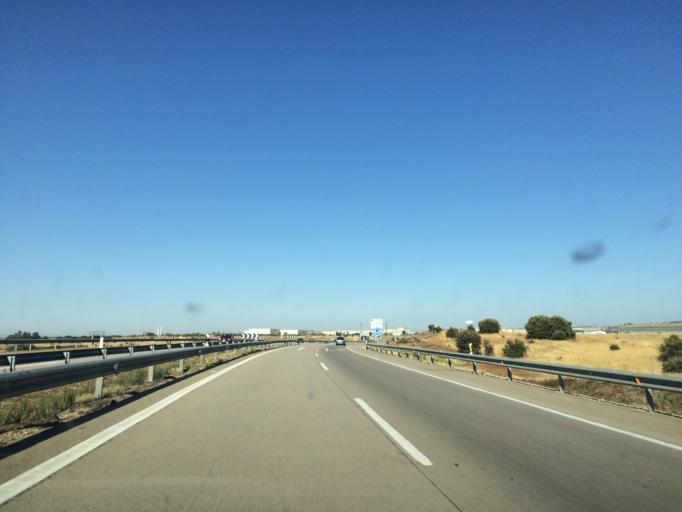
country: ES
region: Castille-La Mancha
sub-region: Province of Toledo
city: Mejorada
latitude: 39.9582
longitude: -4.9087
